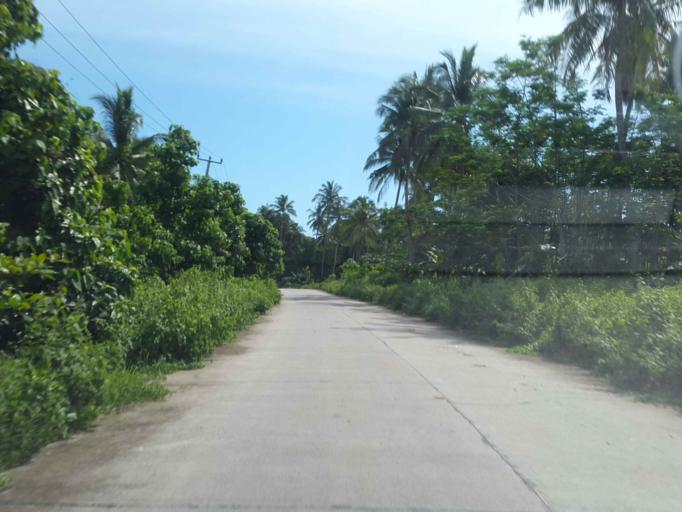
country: ID
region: Banten
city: Babakanbungur
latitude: -6.5305
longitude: 105.6260
